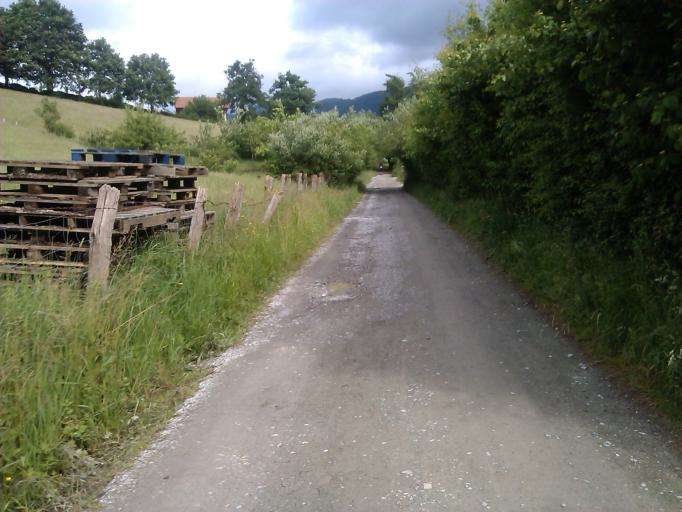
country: ES
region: Navarre
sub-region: Provincia de Navarra
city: Leitza
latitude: 43.0862
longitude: -1.9153
